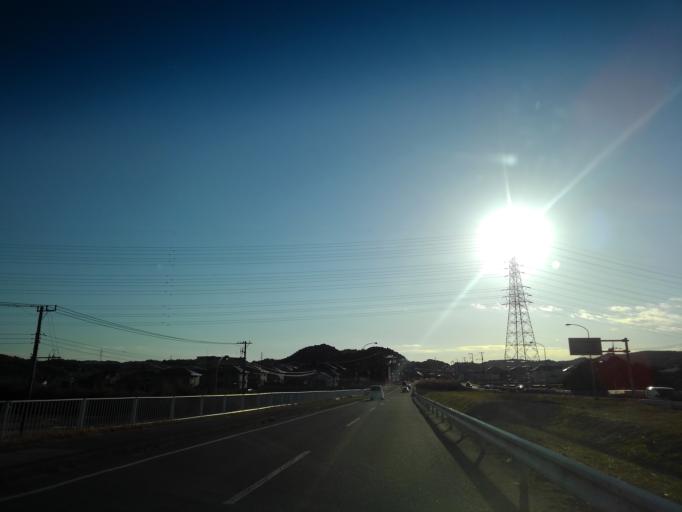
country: JP
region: Chiba
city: Kimitsu
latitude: 35.3118
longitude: 139.9254
